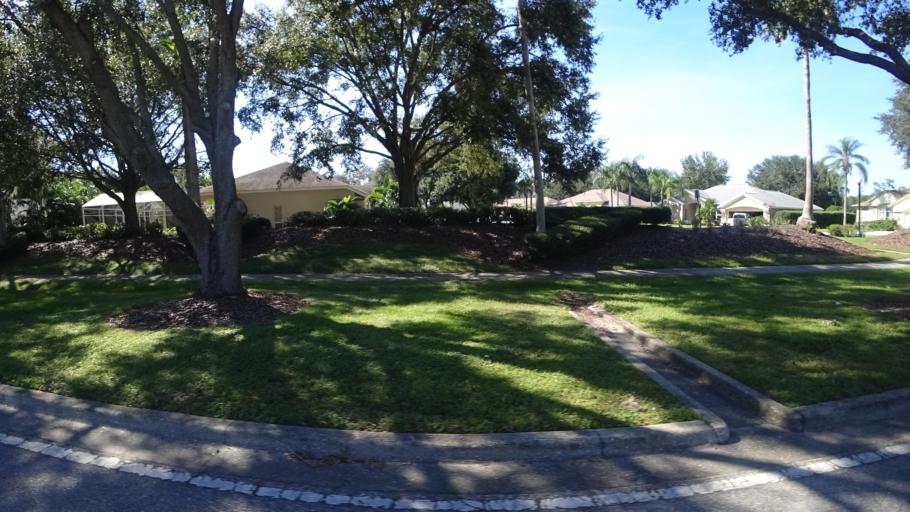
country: US
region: Florida
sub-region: Sarasota County
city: The Meadows
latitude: 27.4312
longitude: -82.4363
